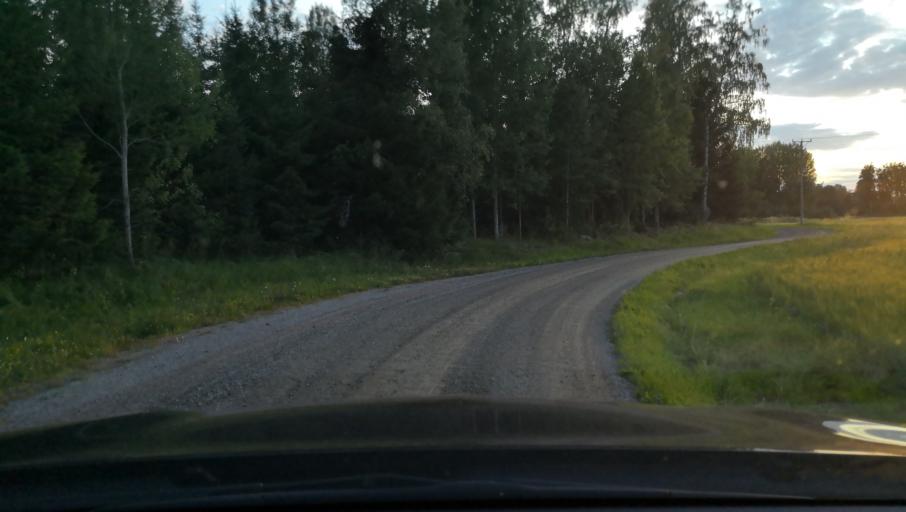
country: SE
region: Uppsala
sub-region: Osthammars Kommun
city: Bjorklinge
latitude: 60.0536
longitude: 17.6326
